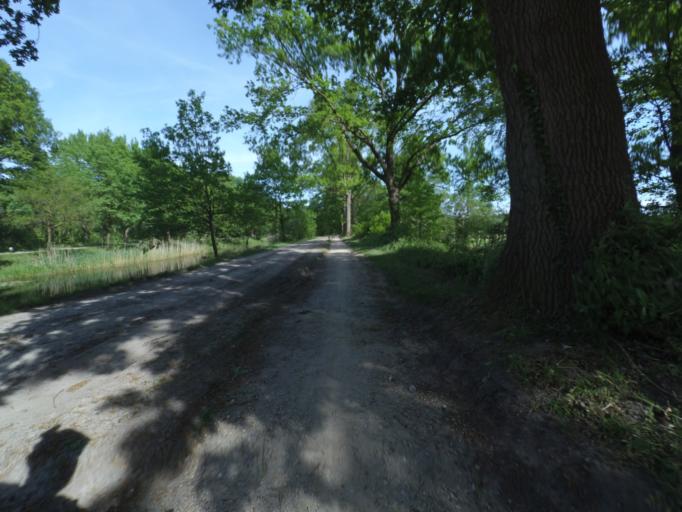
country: NL
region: Overijssel
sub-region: Gemeente Almelo
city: Almelo
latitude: 52.3688
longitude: 6.7076
